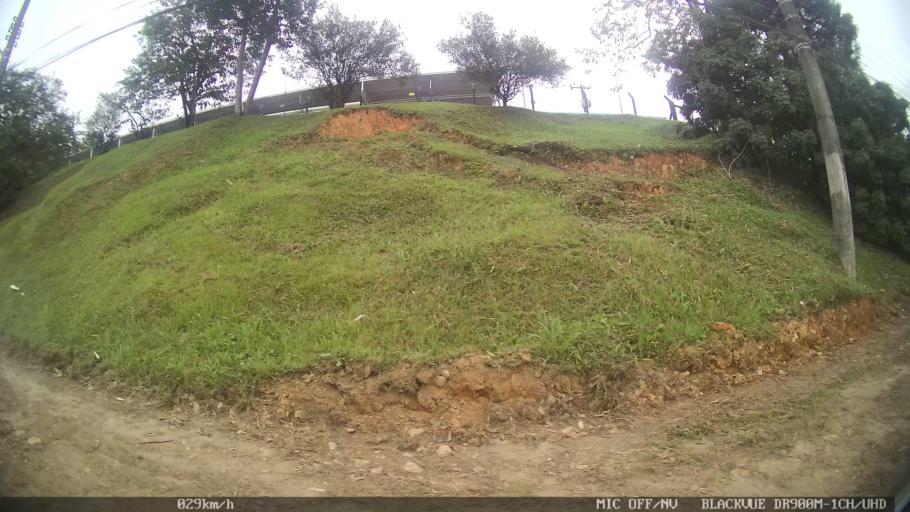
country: BR
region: Santa Catarina
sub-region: Joinville
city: Joinville
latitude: -26.2462
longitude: -48.8822
